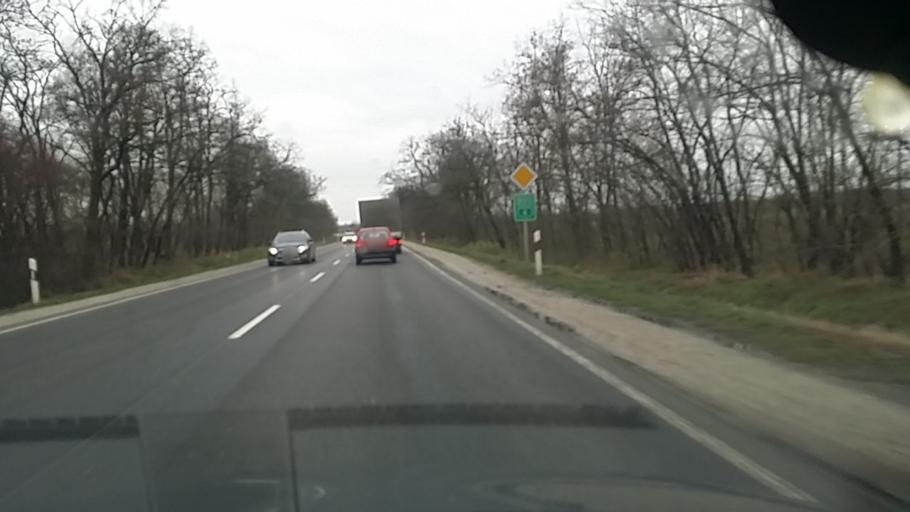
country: HU
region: Szabolcs-Szatmar-Bereg
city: Ujfeherto
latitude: 47.8358
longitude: 21.7034
